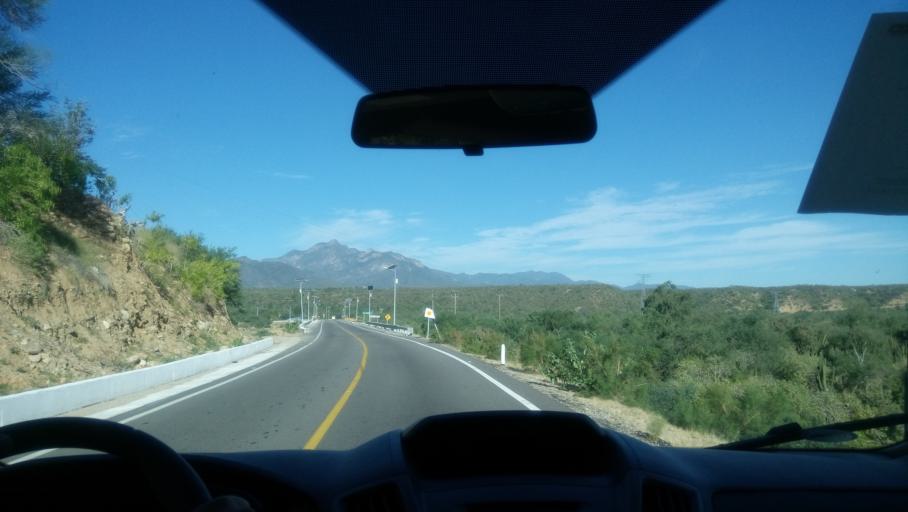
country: MX
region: Baja California Sur
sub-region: Los Cabos
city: Las Veredas
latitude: 23.3304
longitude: -109.7641
